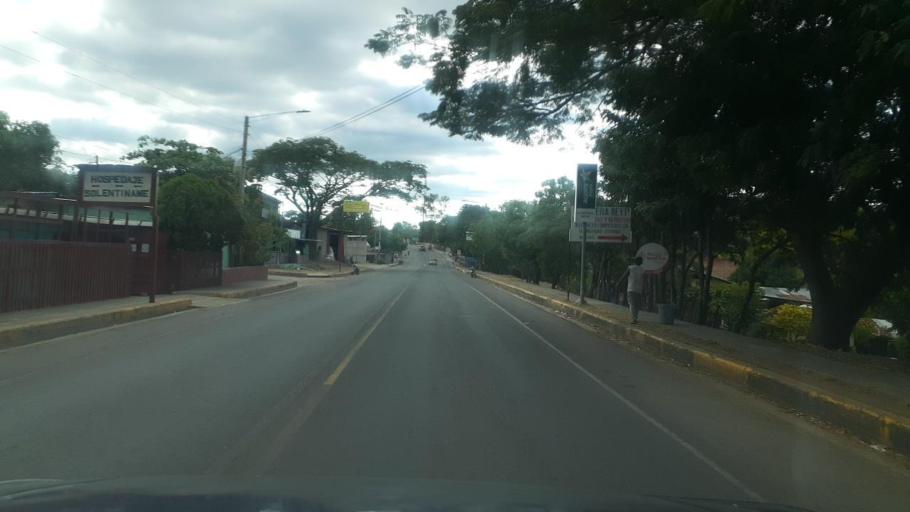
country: NI
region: Madriz
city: Somoto
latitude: 13.4889
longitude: -86.5802
